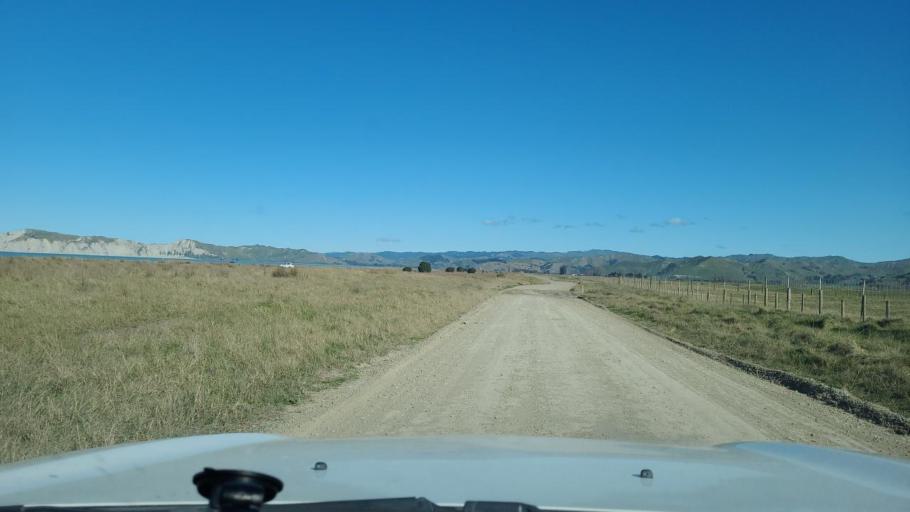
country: NZ
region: Gisborne
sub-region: Gisborne District
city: Gisborne
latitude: -38.7016
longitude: 177.9480
